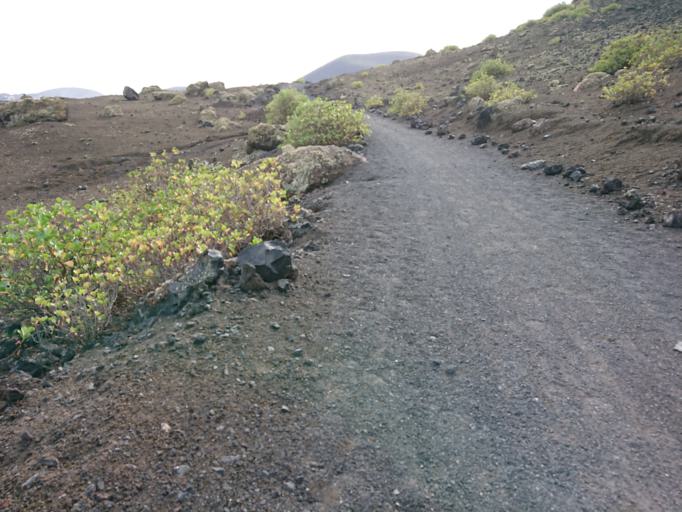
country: ES
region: Canary Islands
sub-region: Provincia de Las Palmas
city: Tias
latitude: 29.0067
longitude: -13.6756
